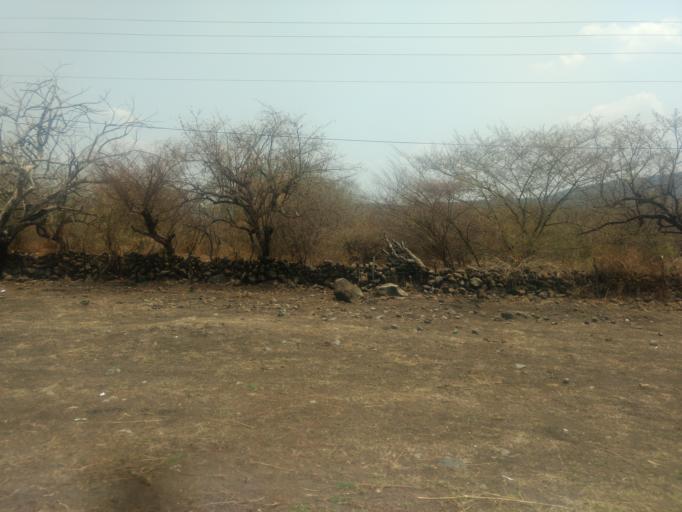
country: MX
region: Morelos
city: La Joya
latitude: 18.6670
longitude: -99.4254
